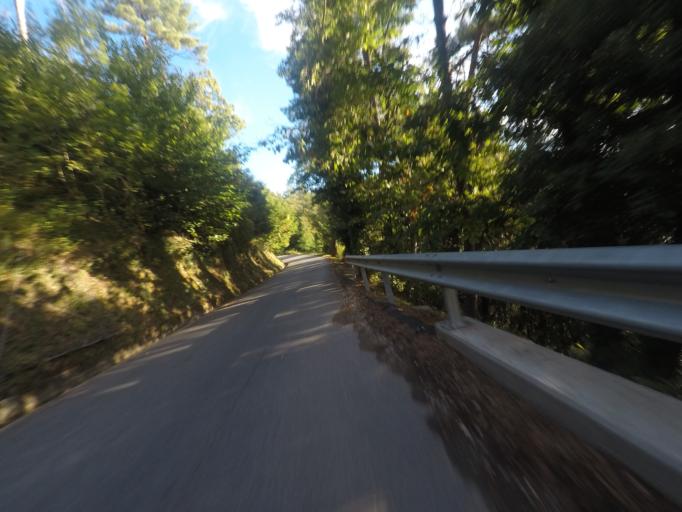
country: IT
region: Tuscany
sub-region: Provincia di Lucca
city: Stiava
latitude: 43.9152
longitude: 10.3682
